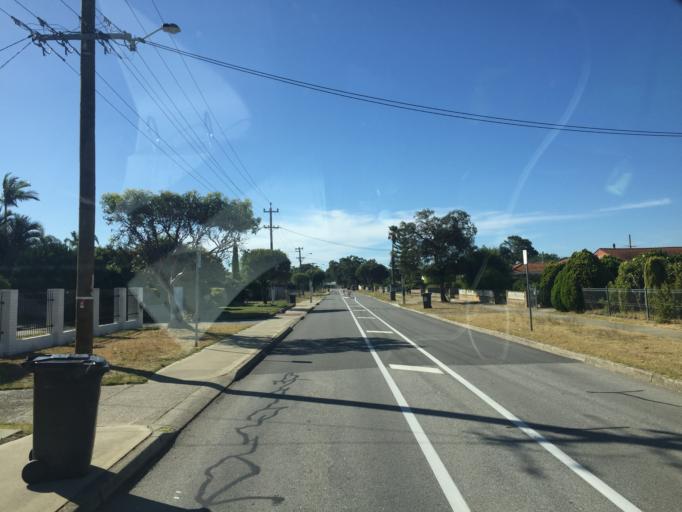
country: AU
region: Western Australia
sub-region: Gosnells
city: Maddington
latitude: -32.0508
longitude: 115.9993
